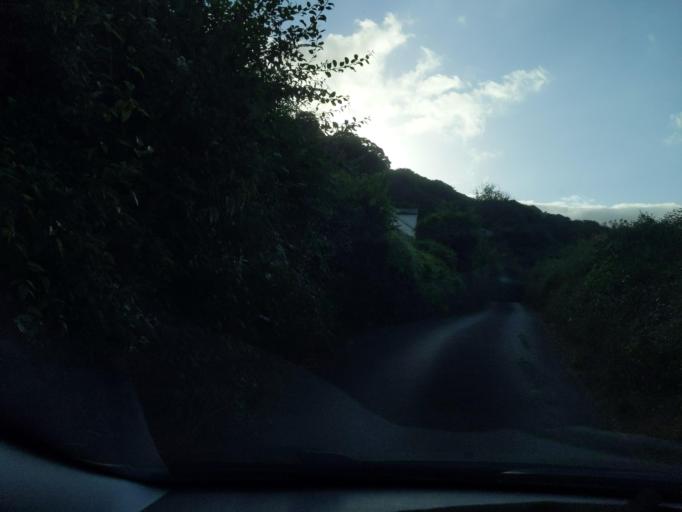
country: GB
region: England
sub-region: Devon
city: Salcombe
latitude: 50.2244
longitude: -3.7872
